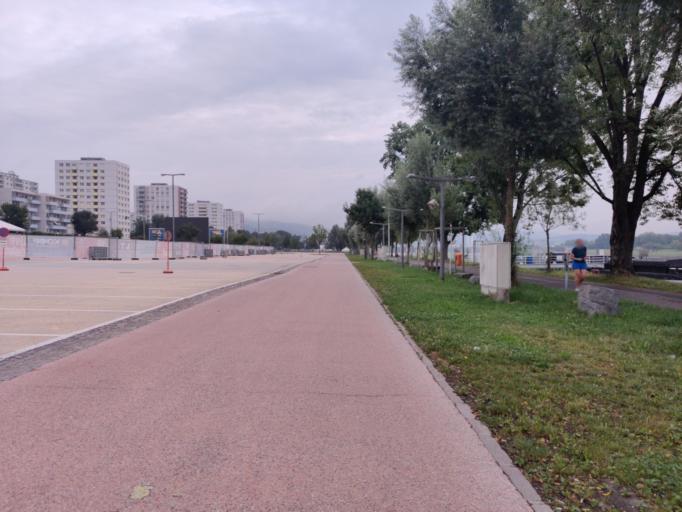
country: AT
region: Upper Austria
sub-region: Linz Stadt
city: Linz
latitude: 48.3122
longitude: 14.2885
